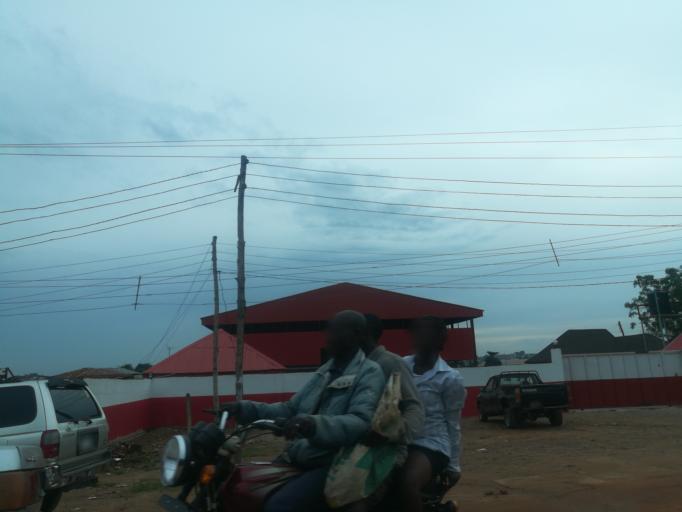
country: NG
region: Oyo
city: Egbeda
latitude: 7.3855
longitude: 3.9956
